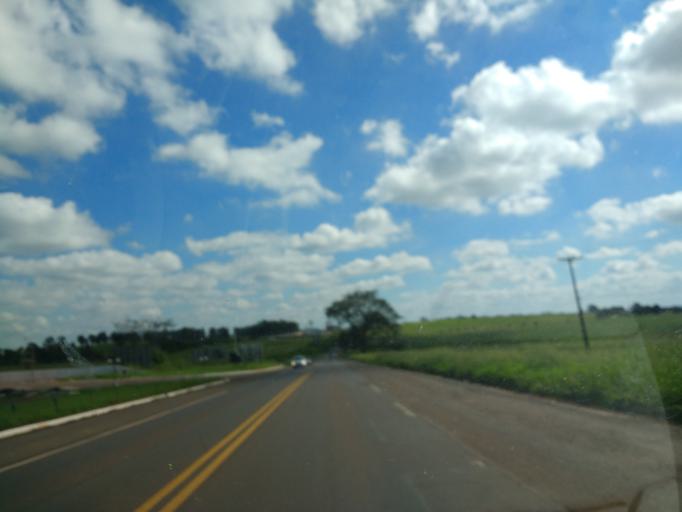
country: BR
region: Parana
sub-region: Alto Piquiri
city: Alto Piquiri
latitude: -23.8916
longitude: -53.4228
